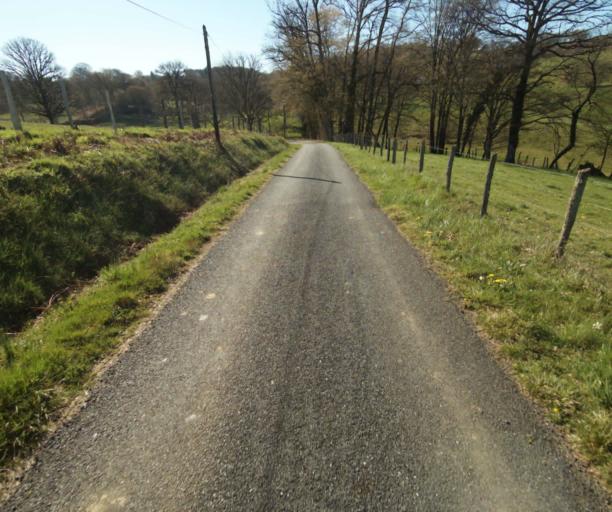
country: FR
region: Limousin
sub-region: Departement de la Correze
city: Chamboulive
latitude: 45.4004
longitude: 1.6992
